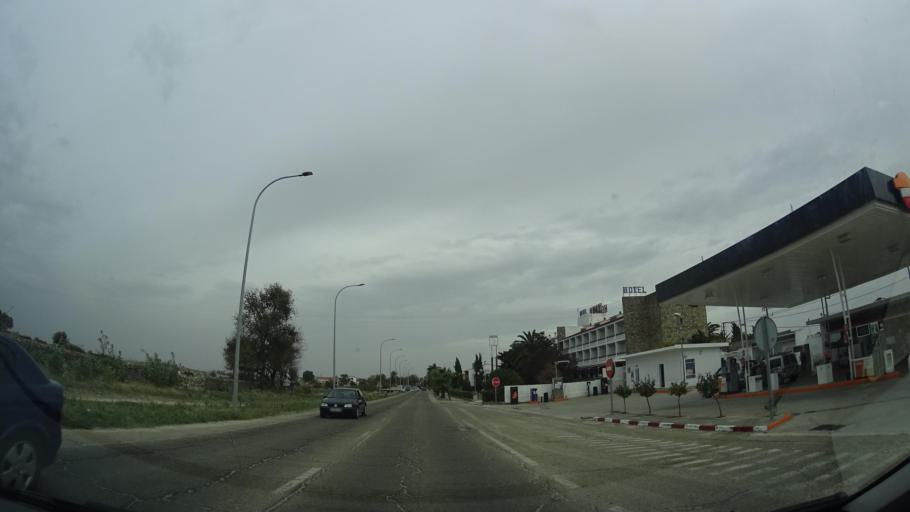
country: ES
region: Extremadura
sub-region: Provincia de Caceres
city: Trujillo
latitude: 39.4604
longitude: -5.8709
